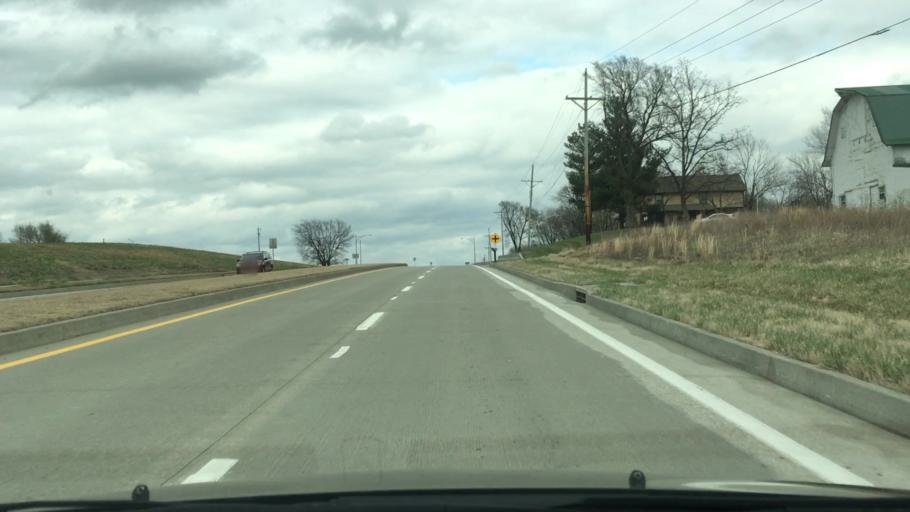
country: US
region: Missouri
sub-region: Cass County
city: Raymore
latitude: 38.8555
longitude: -94.4662
